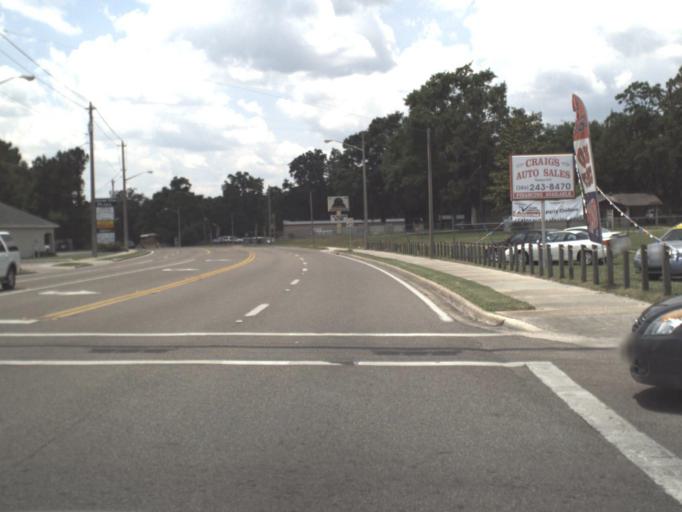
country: US
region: Florida
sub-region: Columbia County
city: Watertown
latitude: 30.1834
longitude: -82.6094
